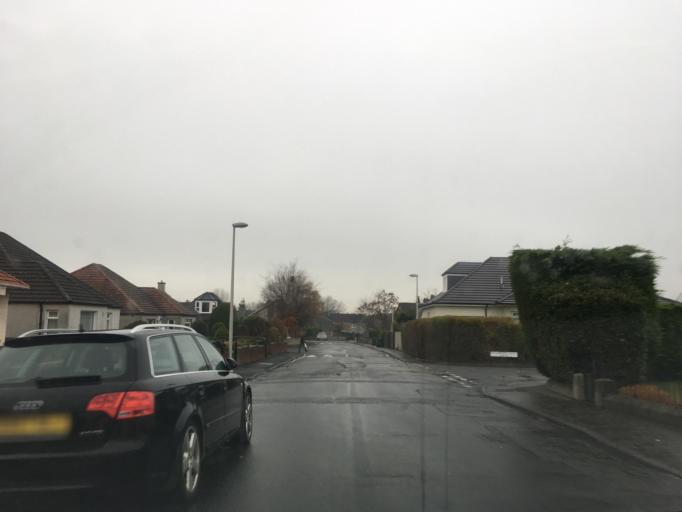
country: GB
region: Scotland
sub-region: Edinburgh
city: Currie
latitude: 55.9480
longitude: -3.2998
